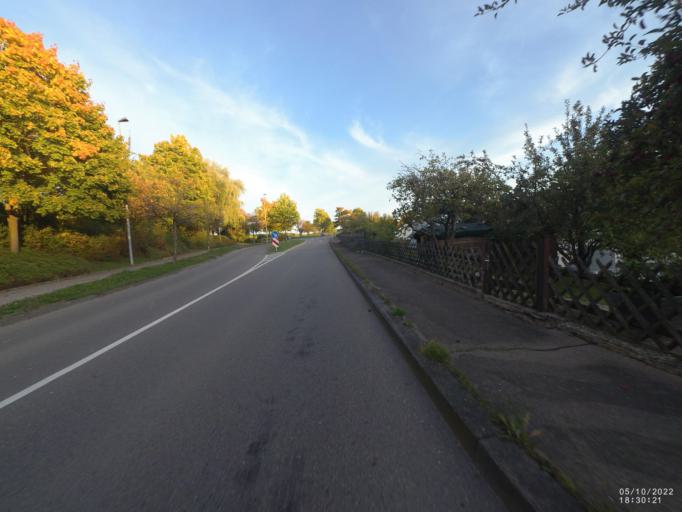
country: DE
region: Baden-Wuerttemberg
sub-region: Regierungsbezirk Stuttgart
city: Ebersbach an der Fils
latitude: 48.7080
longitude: 9.5265
